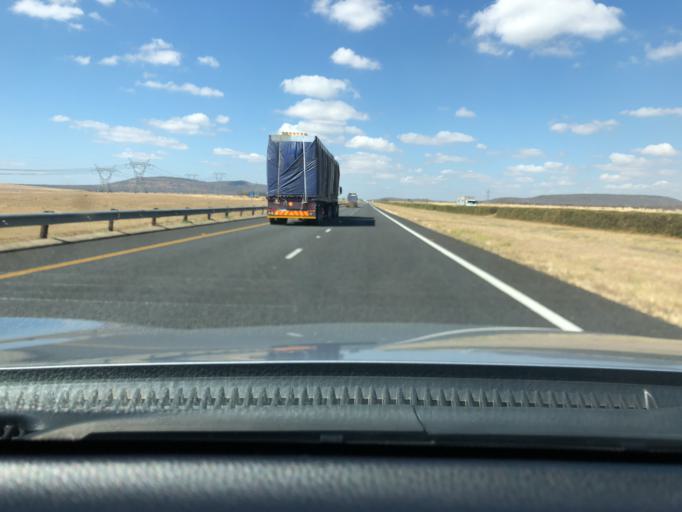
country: ZA
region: KwaZulu-Natal
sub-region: uThukela District Municipality
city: Ladysmith
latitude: -28.7937
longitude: 29.6852
